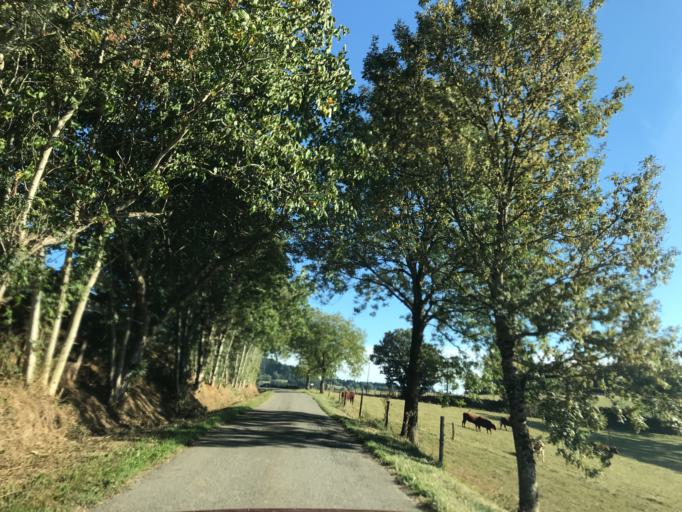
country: FR
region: Auvergne
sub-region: Departement du Puy-de-Dome
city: Escoutoux
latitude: 45.7674
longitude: 3.6266
